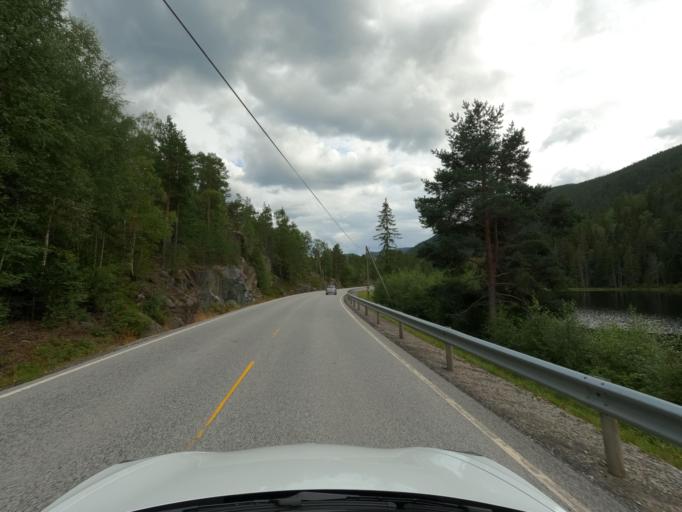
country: NO
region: Telemark
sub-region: Hjartdal
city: Sauland
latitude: 59.8612
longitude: 8.9392
